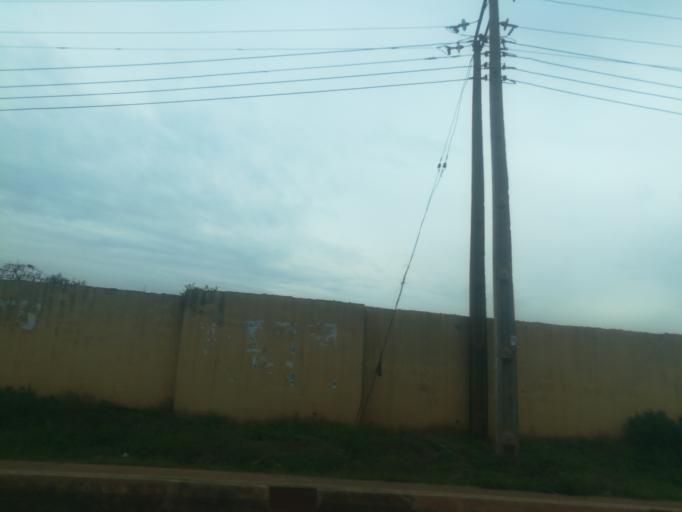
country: NG
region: Oyo
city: Ibadan
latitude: 7.3927
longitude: 3.9263
